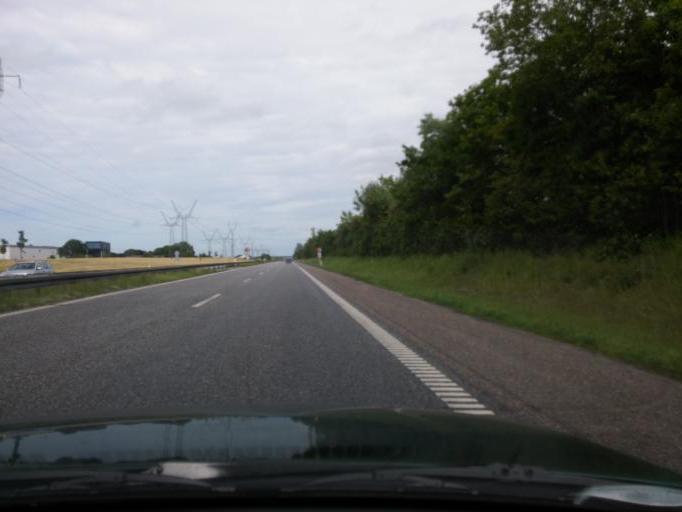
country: DK
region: South Denmark
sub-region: Odense Kommune
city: Neder Holluf
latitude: 55.3563
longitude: 10.4805
